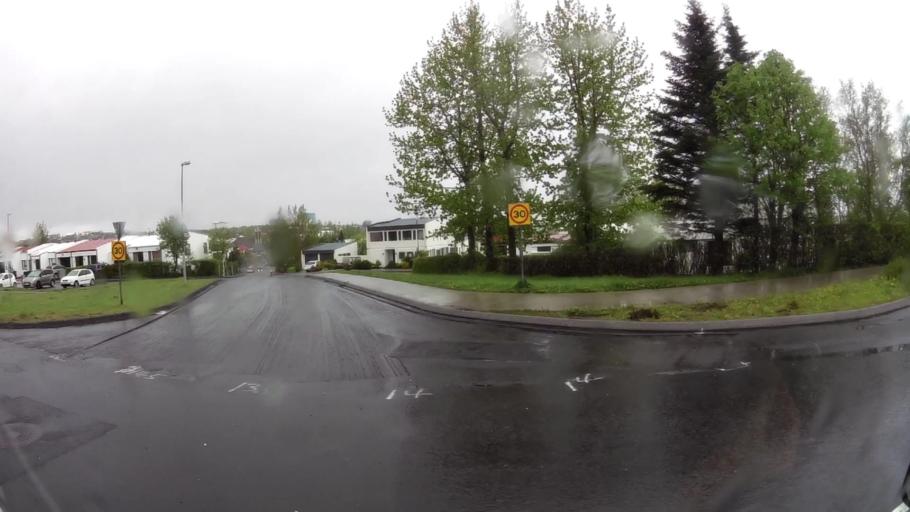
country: IS
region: Capital Region
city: Reykjavik
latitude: 64.1005
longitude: -21.8419
